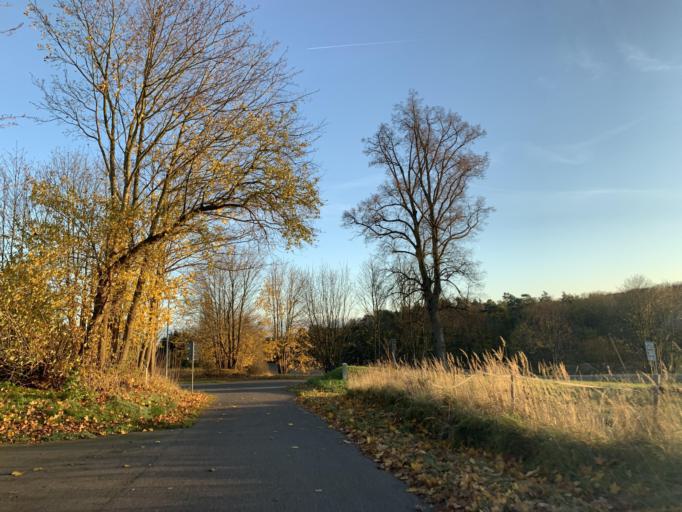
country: DE
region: Mecklenburg-Vorpommern
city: Loitz
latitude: 53.4018
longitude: 13.3654
